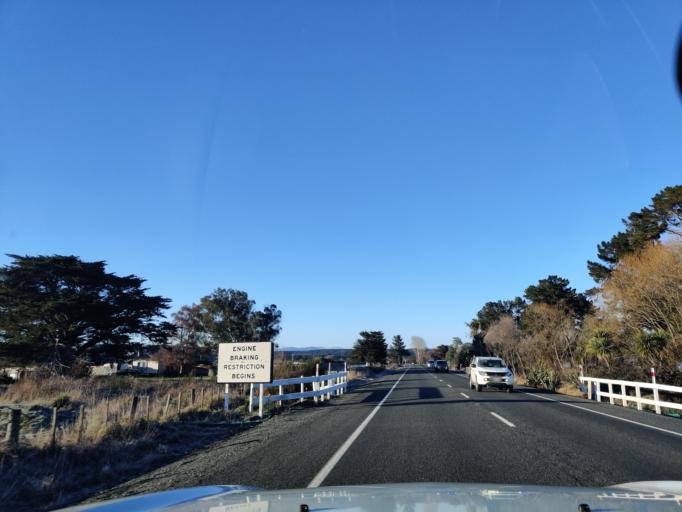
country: NZ
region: Waikato
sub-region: Taupo District
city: Taupo
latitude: -38.7712
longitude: 176.0763
